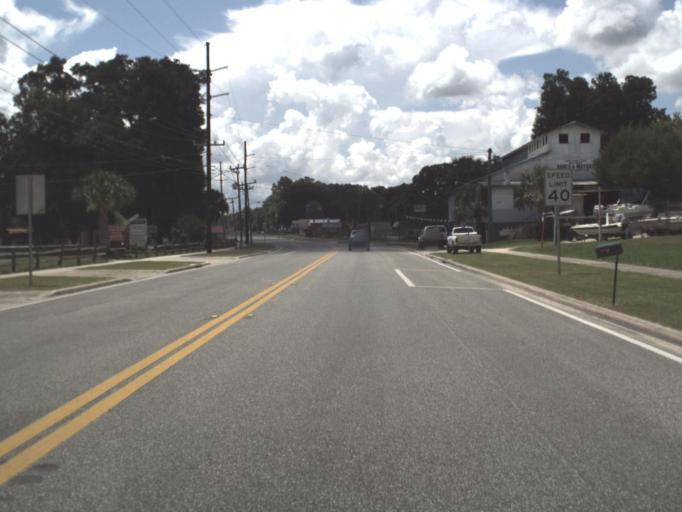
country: US
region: Florida
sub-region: Putnam County
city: Crescent City
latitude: 29.4984
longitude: -81.5969
